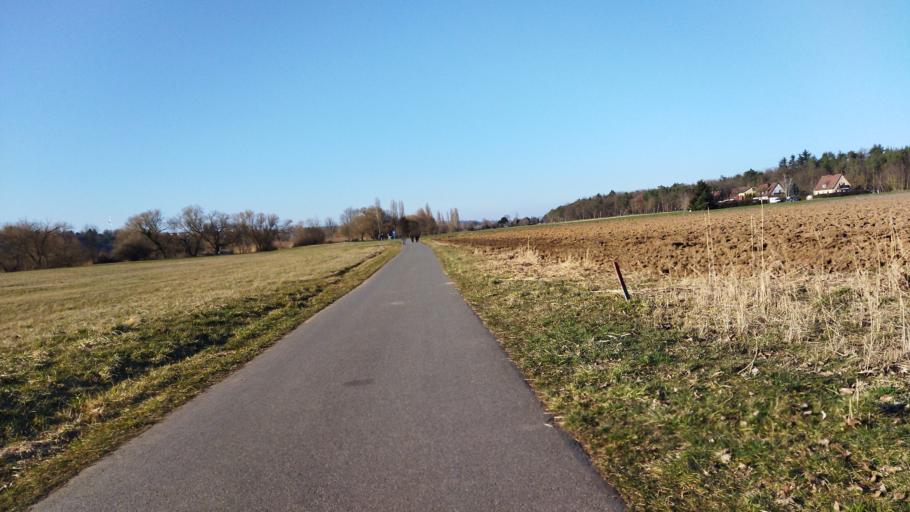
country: DE
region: Bavaria
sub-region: Regierungsbezirk Unterfranken
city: Kitzingen
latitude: 49.7503
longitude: 10.1611
